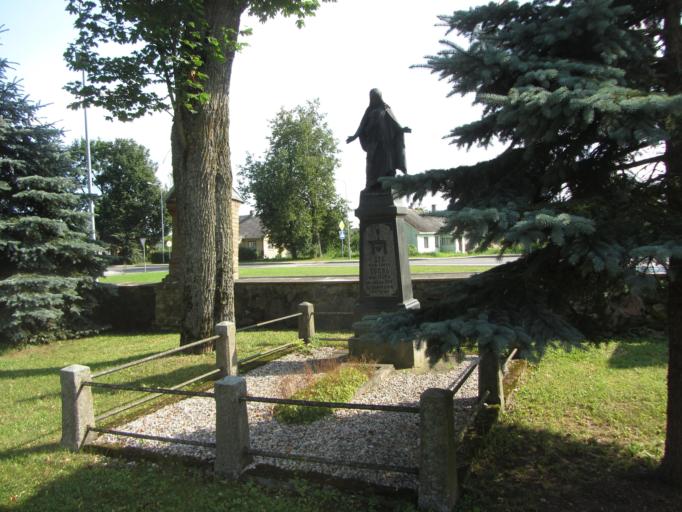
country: LT
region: Vilnius County
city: Ukmerge
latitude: 55.2394
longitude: 24.6713
